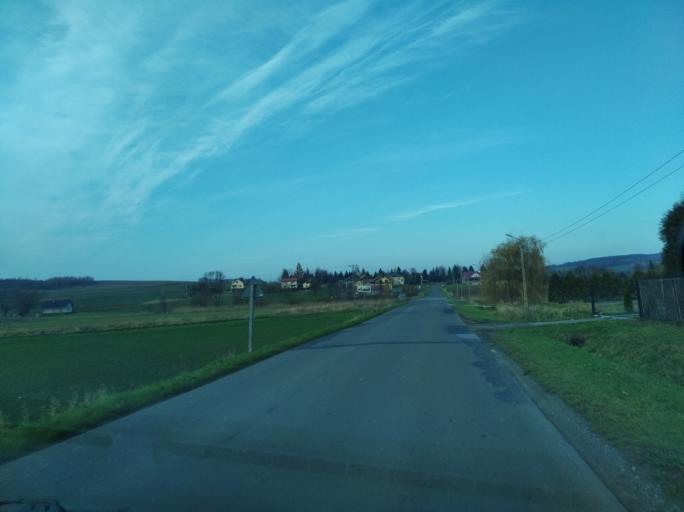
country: PL
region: Subcarpathian Voivodeship
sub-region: Powiat ropczycko-sedziszowski
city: Iwierzyce
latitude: 50.0181
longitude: 21.7526
